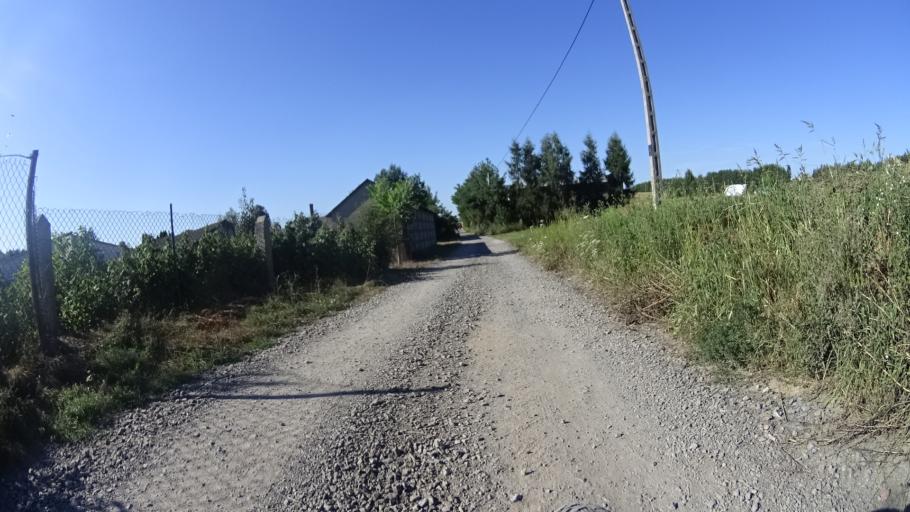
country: PL
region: Masovian Voivodeship
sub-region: Powiat bialobrzeski
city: Wysmierzyce
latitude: 51.6664
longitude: 20.8494
